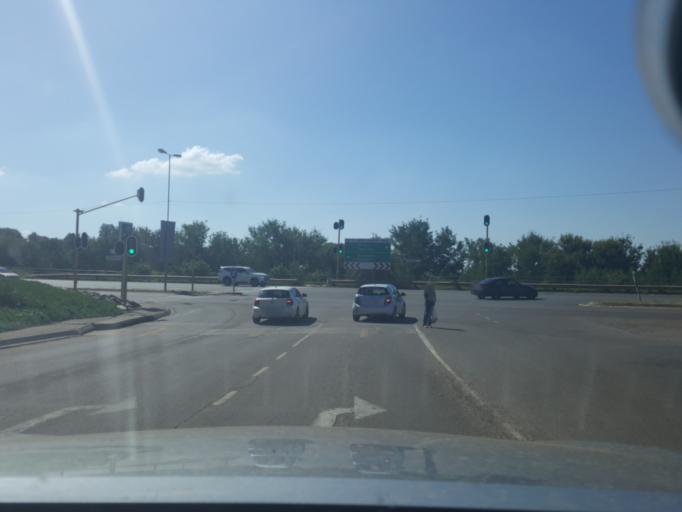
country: ZA
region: Gauteng
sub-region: City of Tshwane Metropolitan Municipality
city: Centurion
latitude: -25.8219
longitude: 28.3138
